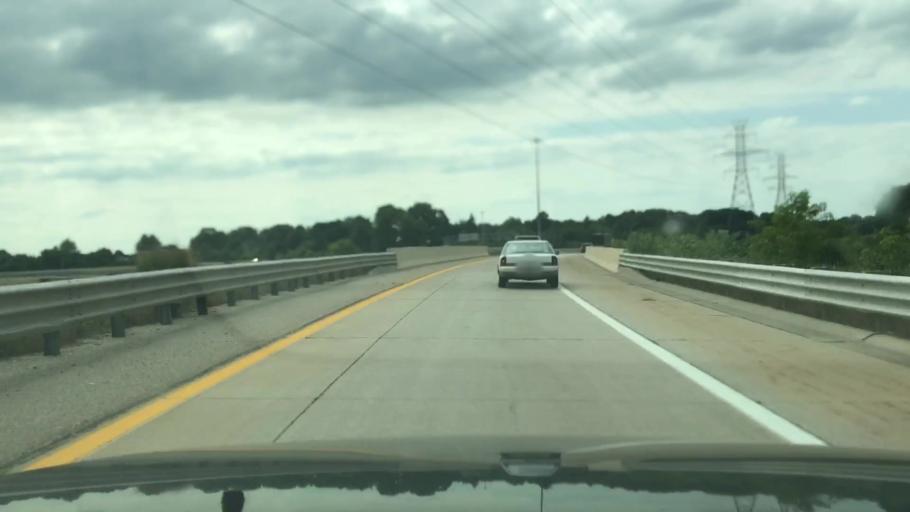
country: US
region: Michigan
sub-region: Kent County
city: Cutlerville
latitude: 42.8499
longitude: -85.6825
